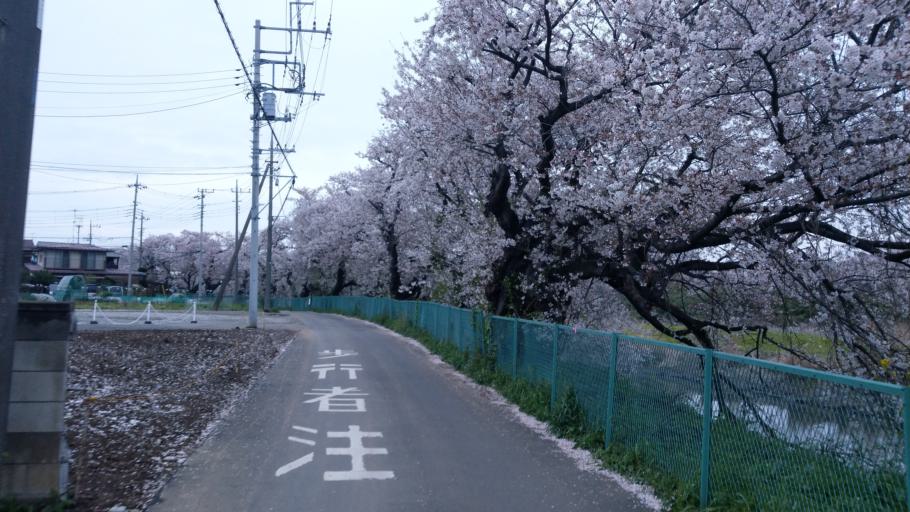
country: JP
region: Saitama
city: Yono
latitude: 35.8926
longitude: 139.5971
